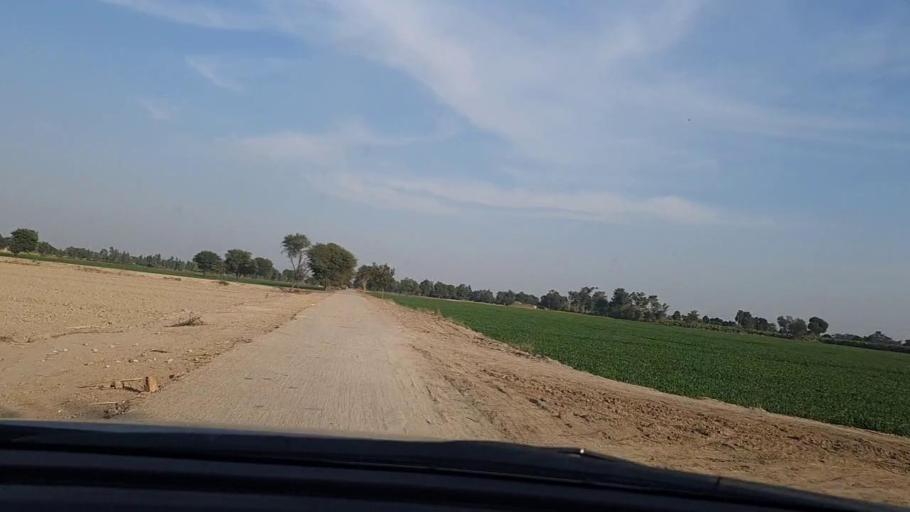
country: PK
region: Sindh
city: Daulatpur
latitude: 26.3369
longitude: 68.0333
